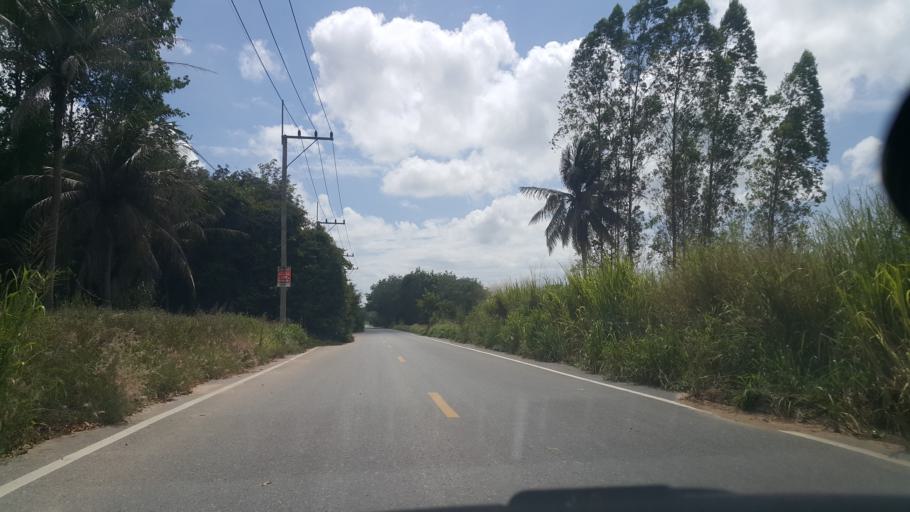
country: TH
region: Rayong
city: Ban Chang
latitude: 12.8082
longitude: 101.0052
